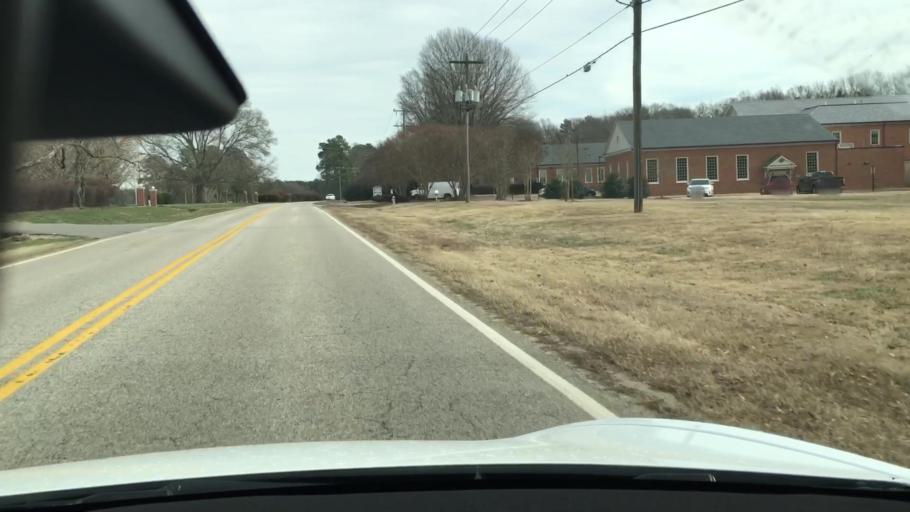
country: US
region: Virginia
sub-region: Chesterfield County
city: Brandermill
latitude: 37.5269
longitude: -77.6548
